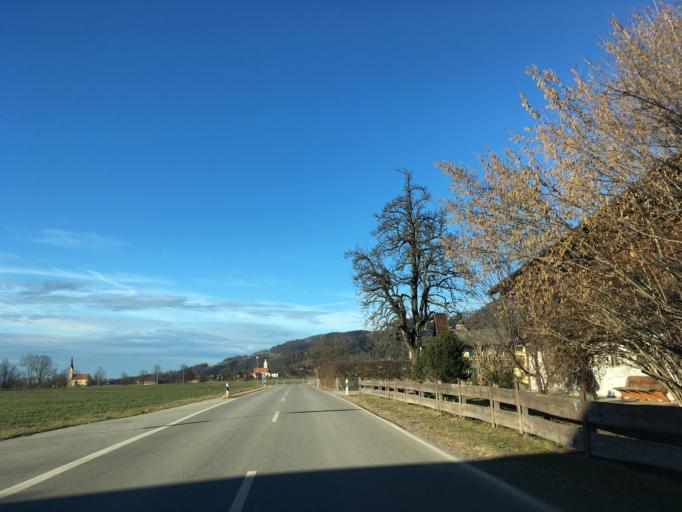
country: DE
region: Bavaria
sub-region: Upper Bavaria
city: Nussdorf am Inn
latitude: 47.7314
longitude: 12.1611
